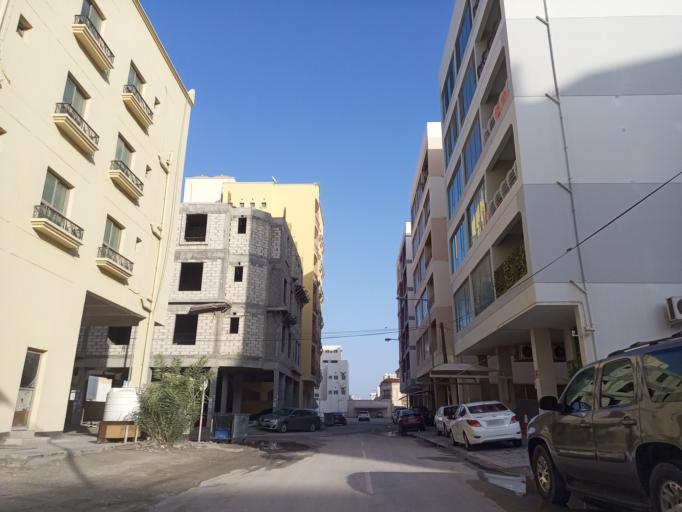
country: BH
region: Muharraq
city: Al Hadd
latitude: 26.2318
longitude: 50.6468
